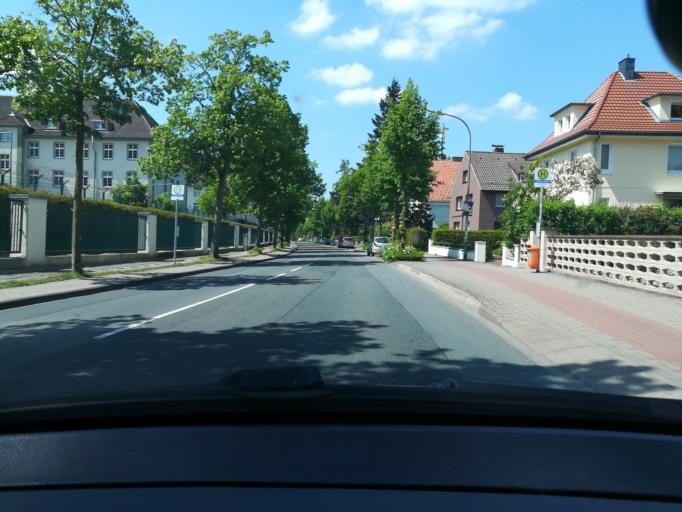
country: DE
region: North Rhine-Westphalia
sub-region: Regierungsbezirk Detmold
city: Herford
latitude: 52.1154
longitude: 8.6945
